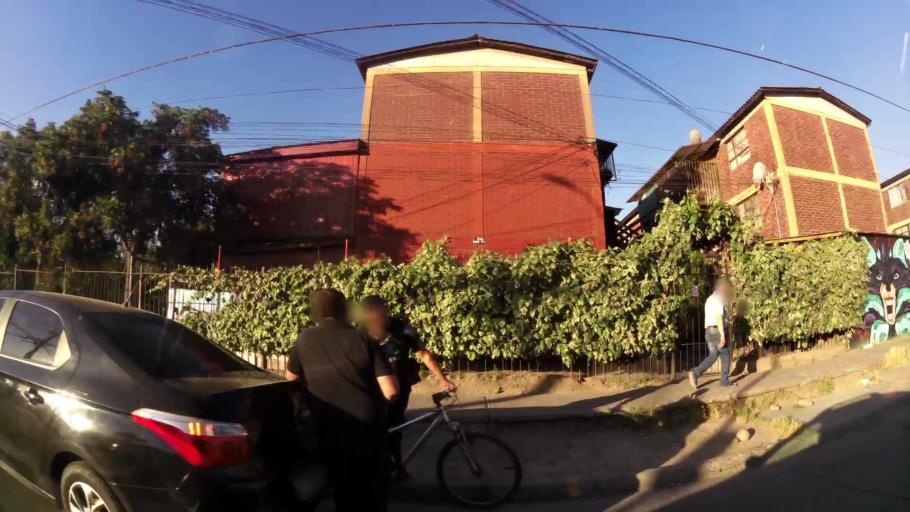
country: CL
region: Santiago Metropolitan
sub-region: Provincia de Maipo
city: San Bernardo
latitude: -33.5805
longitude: -70.6907
